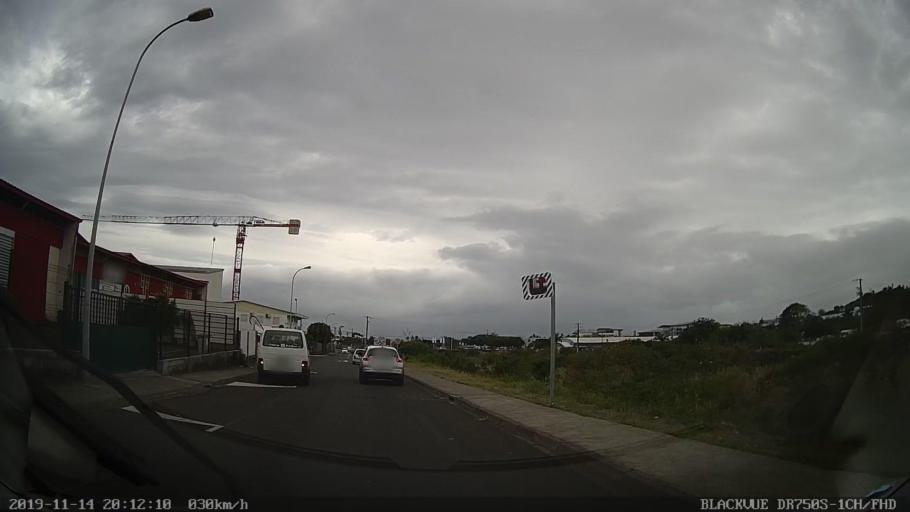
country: RE
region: Reunion
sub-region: Reunion
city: Saint-Denis
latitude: -20.9034
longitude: 55.4956
